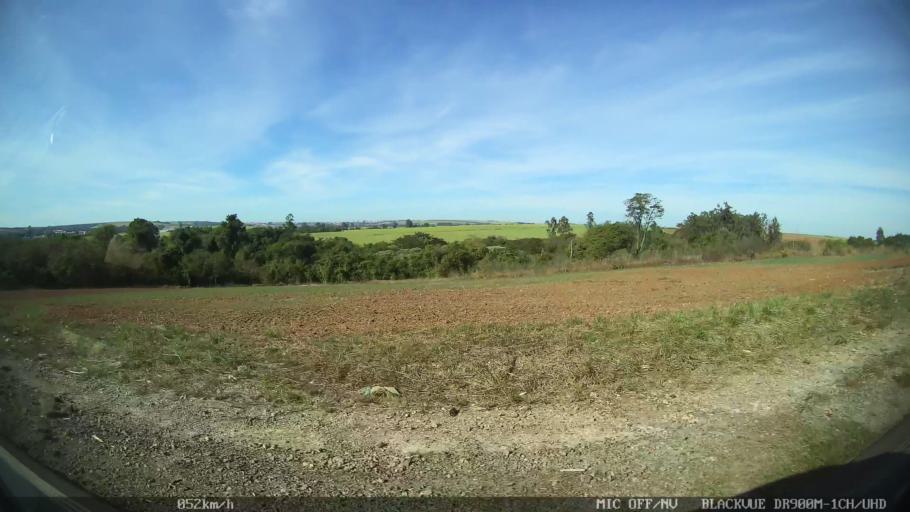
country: BR
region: Sao Paulo
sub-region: Rio Das Pedras
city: Rio das Pedras
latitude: -22.7889
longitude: -47.6349
